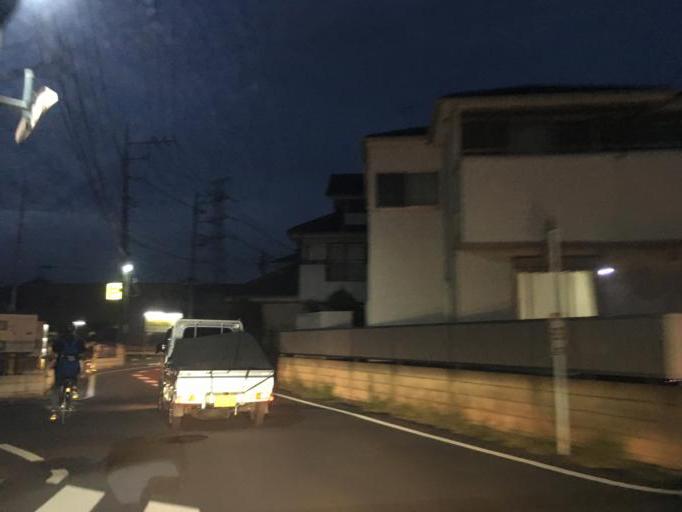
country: JP
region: Tokyo
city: Higashimurayama-shi
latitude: 35.7466
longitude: 139.4514
